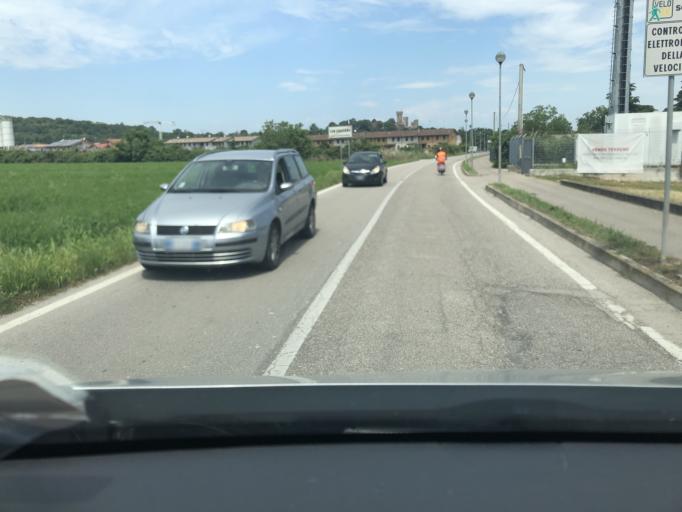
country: IT
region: Veneto
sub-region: Provincia di Verona
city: Valeggio sul Mincio
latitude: 45.3440
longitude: 10.7342
